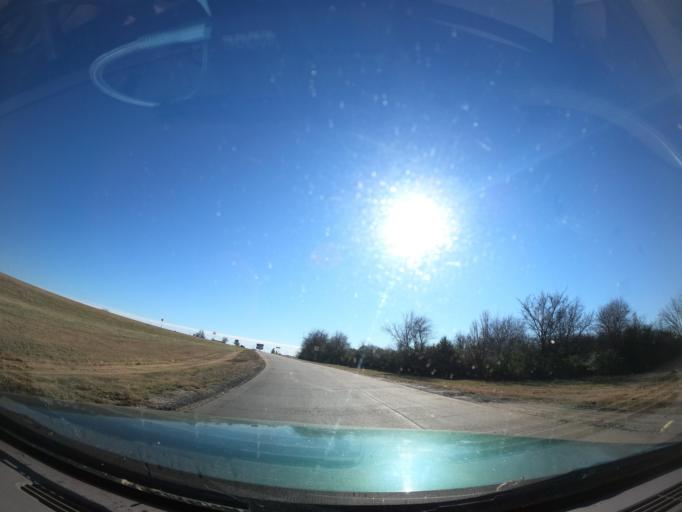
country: US
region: Oklahoma
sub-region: McIntosh County
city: Checotah
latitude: 35.4747
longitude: -95.5376
